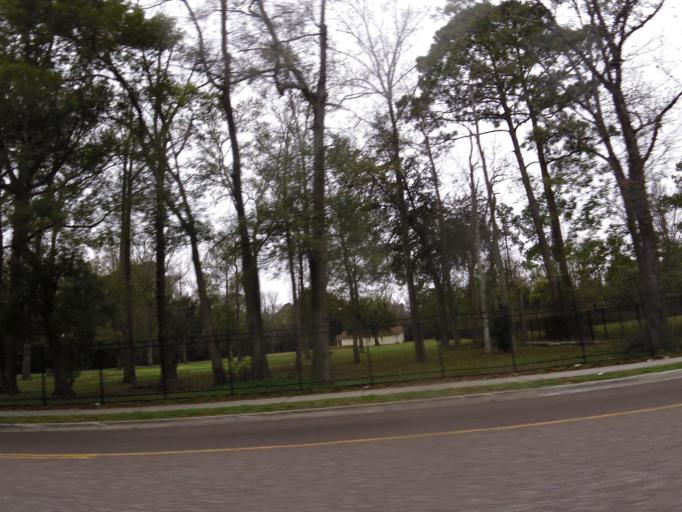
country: US
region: Florida
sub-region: Duval County
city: Jacksonville
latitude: 30.3704
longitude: -81.6990
